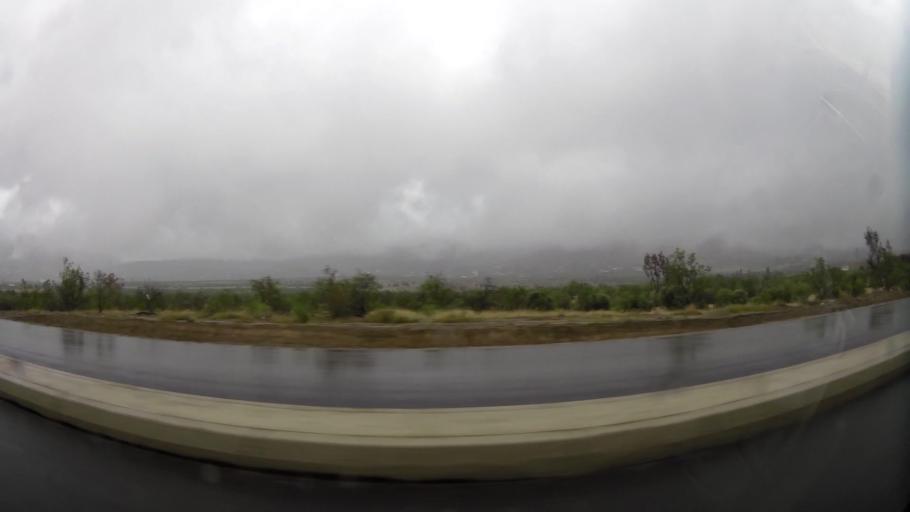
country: MA
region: Oriental
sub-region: Nador
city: Midar
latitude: 34.8242
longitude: -3.7230
